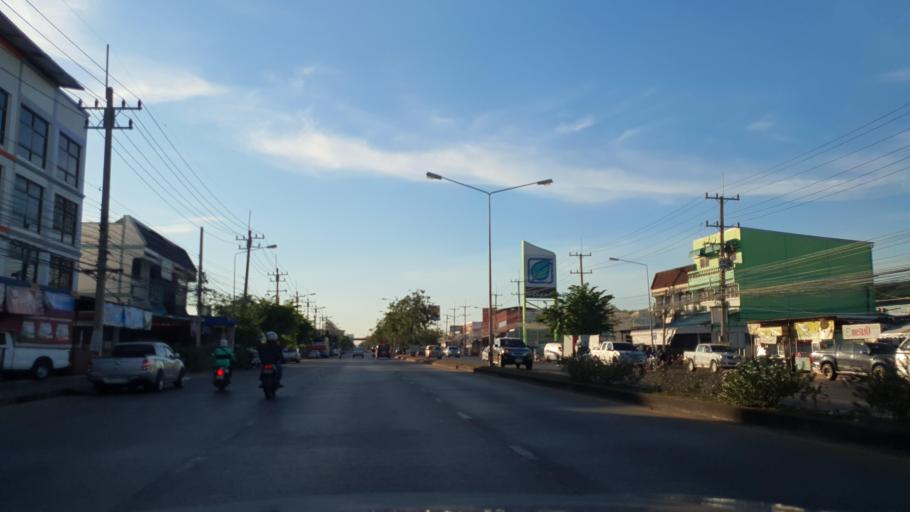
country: TH
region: Khon Kaen
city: Khon Kaen
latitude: 16.4266
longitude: 102.8771
